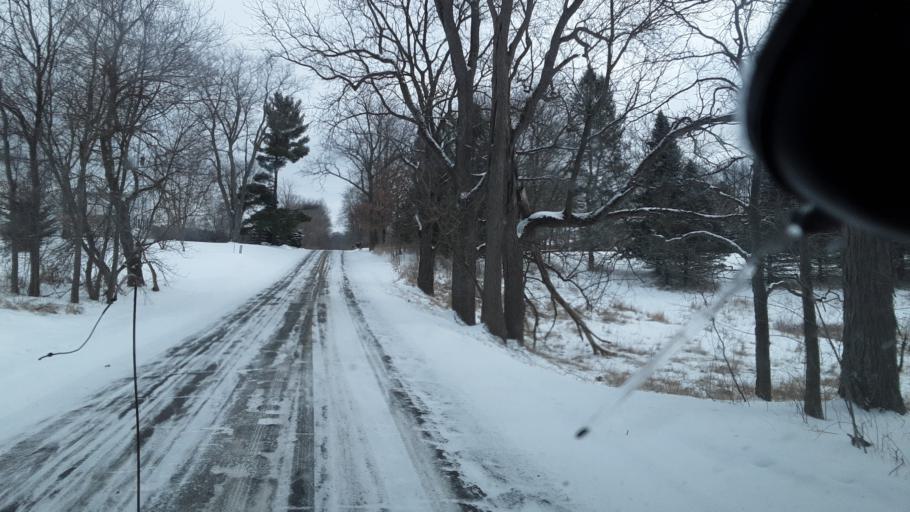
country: US
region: Michigan
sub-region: Ingham County
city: Leslie
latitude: 42.5021
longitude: -84.3787
